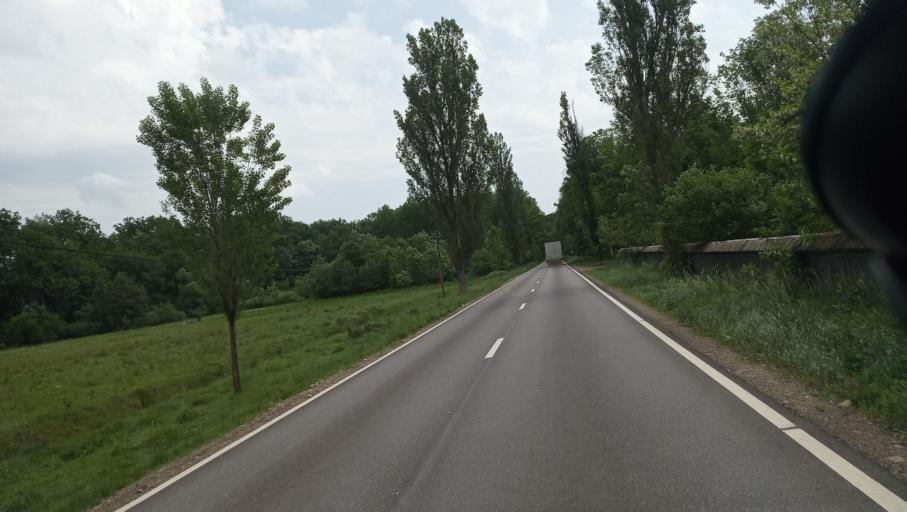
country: RO
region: Neamt
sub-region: Comuna Vanatori Neamt
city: Nemtisor
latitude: 47.2334
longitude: 26.2260
